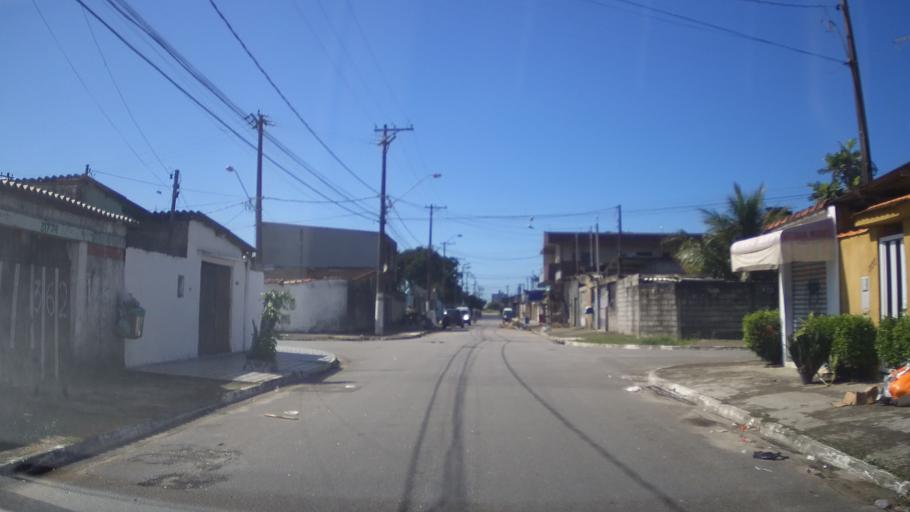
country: BR
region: Sao Paulo
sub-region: Mongagua
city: Mongagua
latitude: -24.0342
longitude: -46.5185
